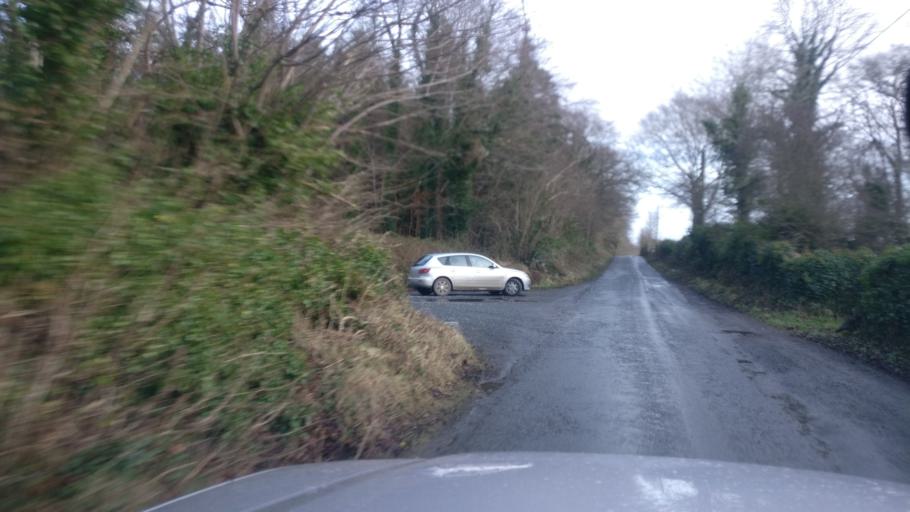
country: IE
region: Connaught
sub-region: County Galway
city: Athenry
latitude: 53.2565
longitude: -8.7173
